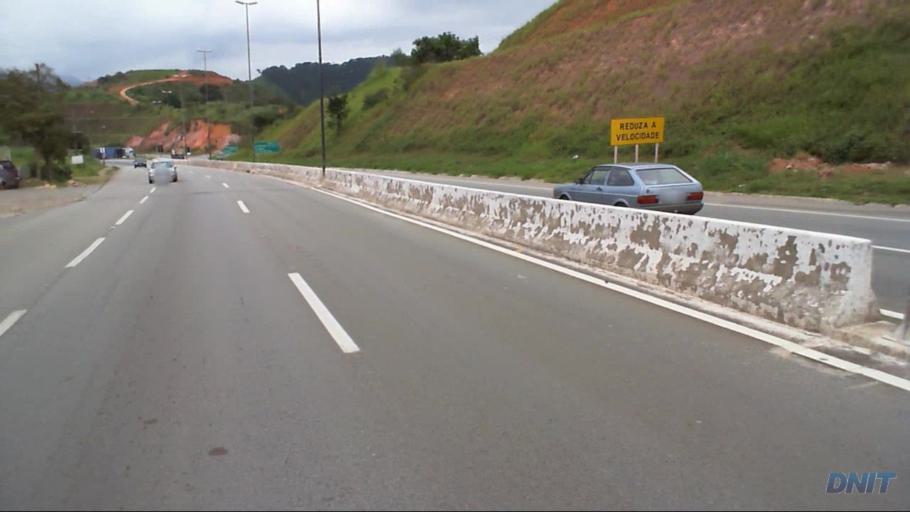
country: BR
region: Minas Gerais
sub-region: Nova Era
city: Nova Era
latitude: -19.7588
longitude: -43.0287
